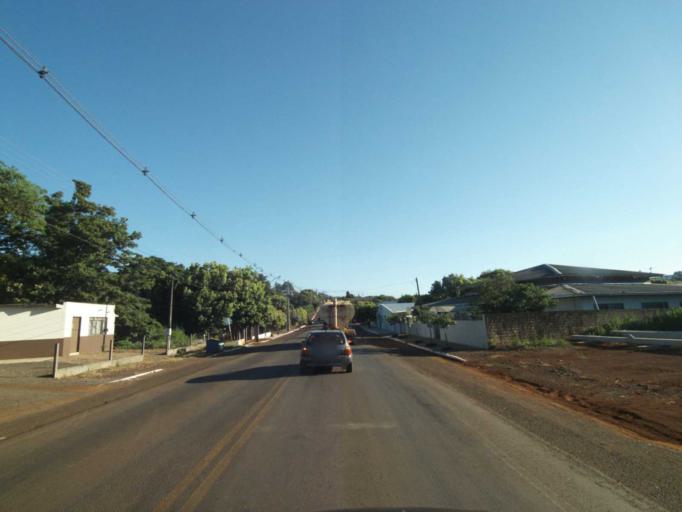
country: BR
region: Parana
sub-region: Coronel Vivida
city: Coronel Vivida
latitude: -25.9661
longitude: -52.8136
